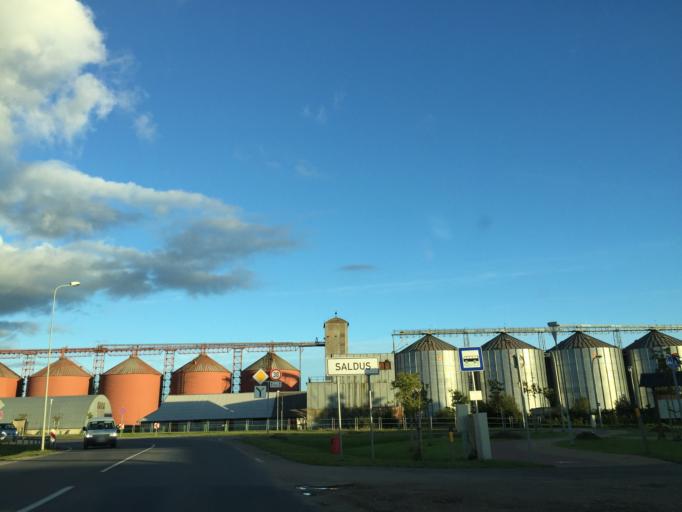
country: LV
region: Saldus Rajons
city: Saldus
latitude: 56.6855
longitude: 22.4623
